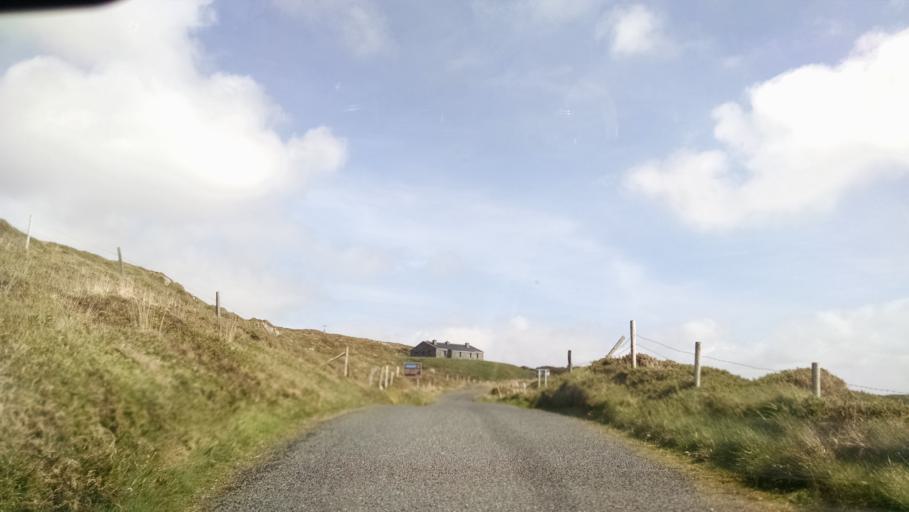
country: IE
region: Connaught
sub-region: County Galway
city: Clifden
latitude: 53.5025
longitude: -10.0991
